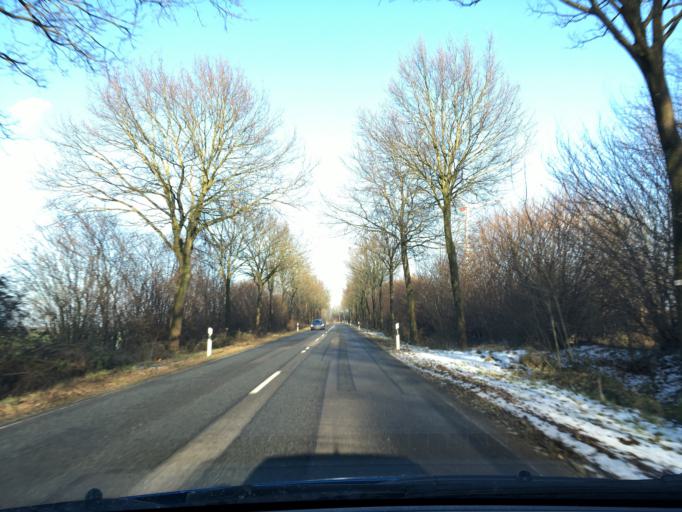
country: DE
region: Schleswig-Holstein
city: Wangelau
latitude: 53.4559
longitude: 10.5544
